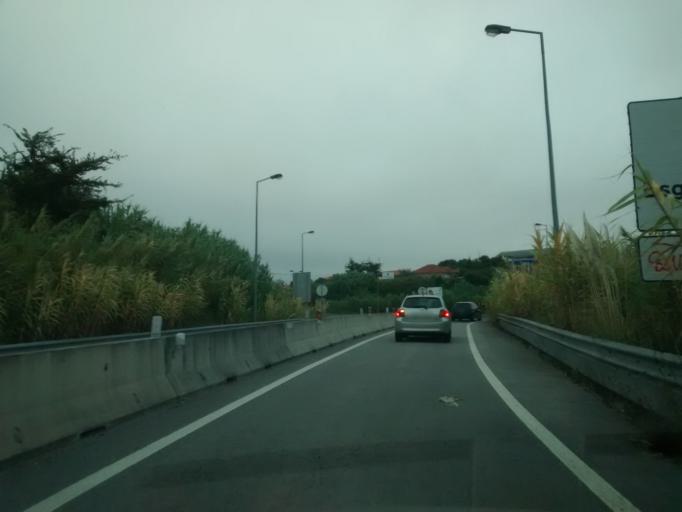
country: PT
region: Aveiro
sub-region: Aveiro
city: Aveiro
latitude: 40.6521
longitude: -8.6422
